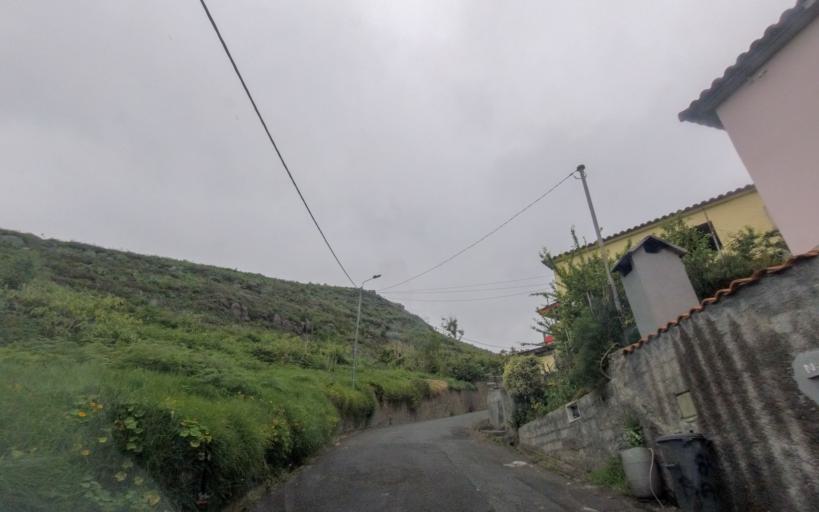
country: PT
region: Madeira
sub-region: Funchal
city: Nossa Senhora do Monte
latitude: 32.6777
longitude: -16.9144
